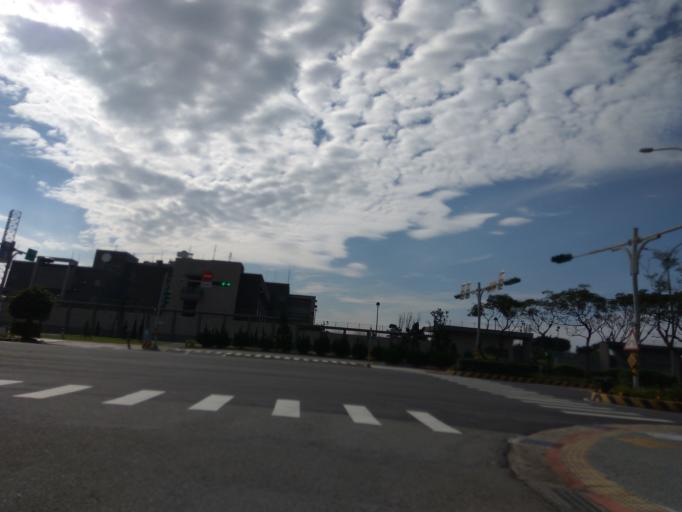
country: TW
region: Taiwan
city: Taoyuan City
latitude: 25.0586
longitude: 121.1771
